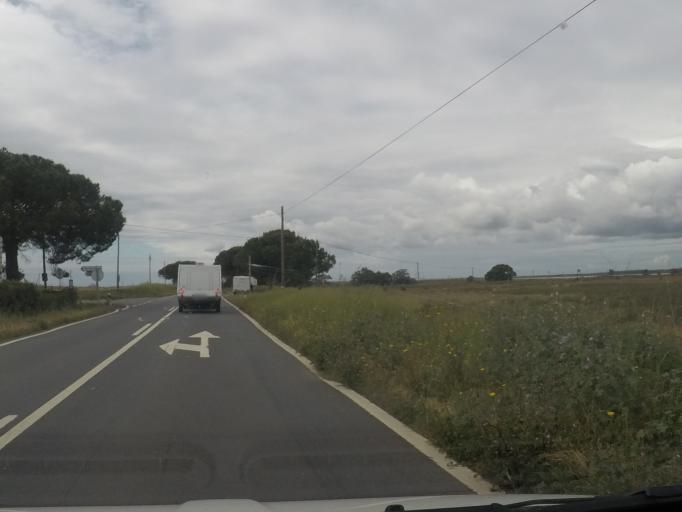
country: PT
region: Setubal
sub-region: Sines
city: Porto Covo
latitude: 37.8874
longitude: -8.7554
